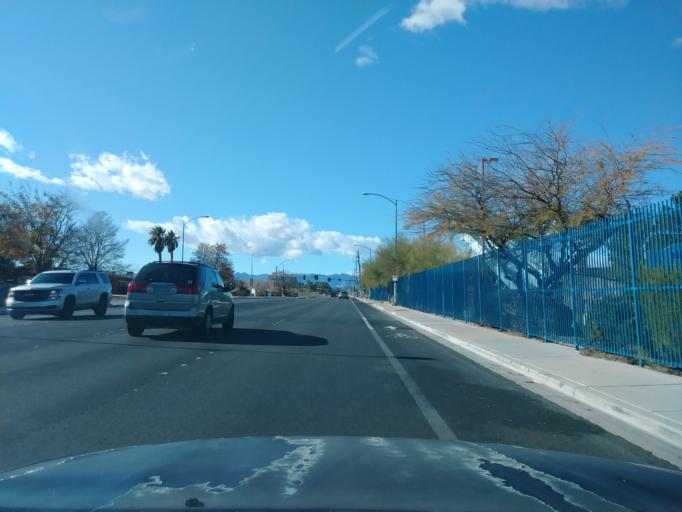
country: US
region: Nevada
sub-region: Clark County
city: Spring Valley
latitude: 36.1518
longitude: -115.2323
